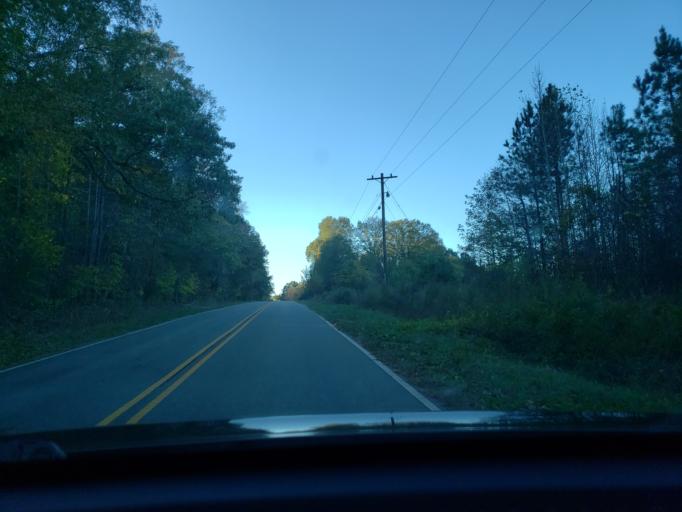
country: US
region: North Carolina
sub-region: Forsyth County
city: Walkertown
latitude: 36.2208
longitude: -80.1871
